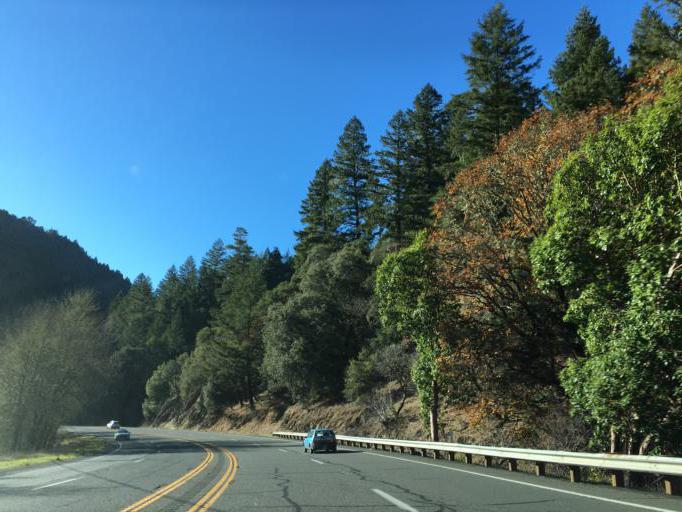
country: US
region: California
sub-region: Mendocino County
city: Brooktrails
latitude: 39.5363
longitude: -123.4074
